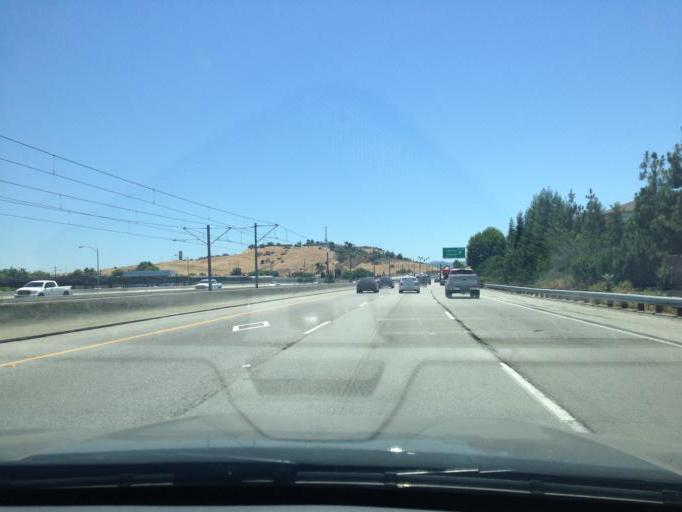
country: US
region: California
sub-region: Santa Clara County
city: Seven Trees
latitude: 37.2994
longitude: -121.8753
